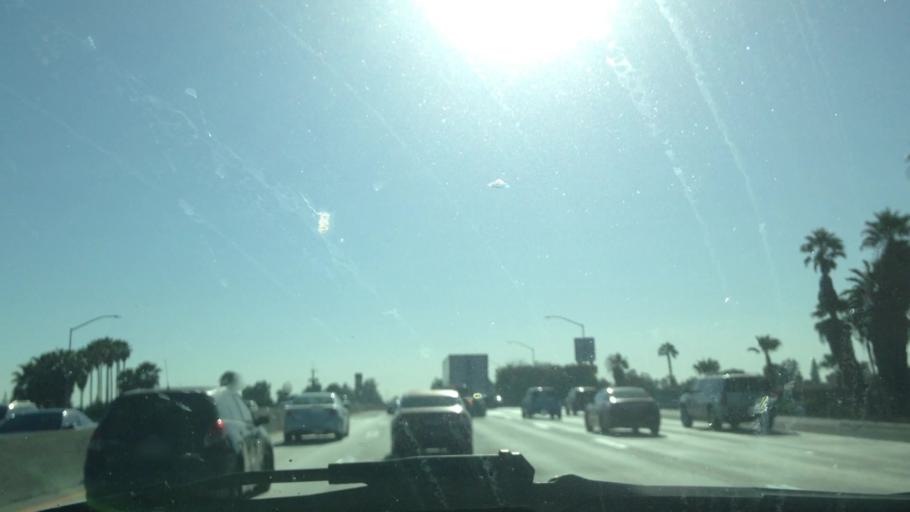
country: US
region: California
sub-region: Los Angeles County
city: Artesia
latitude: 33.8754
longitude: -118.0837
